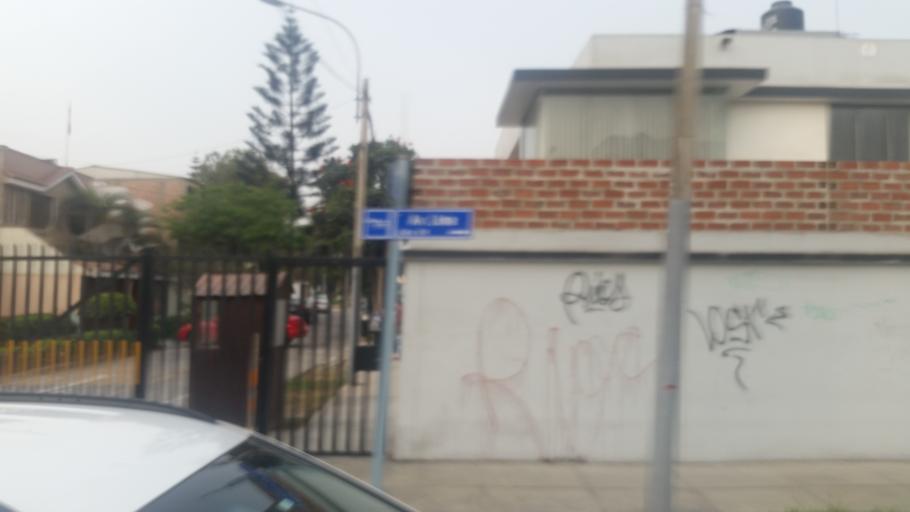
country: PE
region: Lima
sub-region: Lima
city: San Isidro
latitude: -12.0896
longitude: -77.0786
